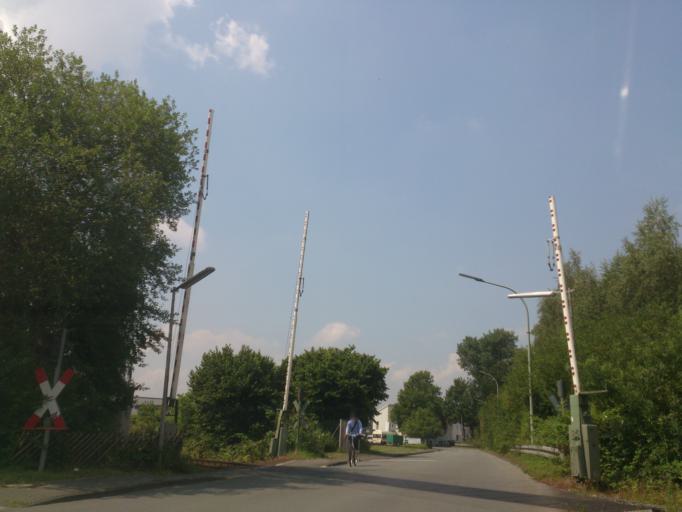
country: DE
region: North Rhine-Westphalia
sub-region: Regierungsbezirk Detmold
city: Paderborn
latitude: 51.7091
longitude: 8.7277
